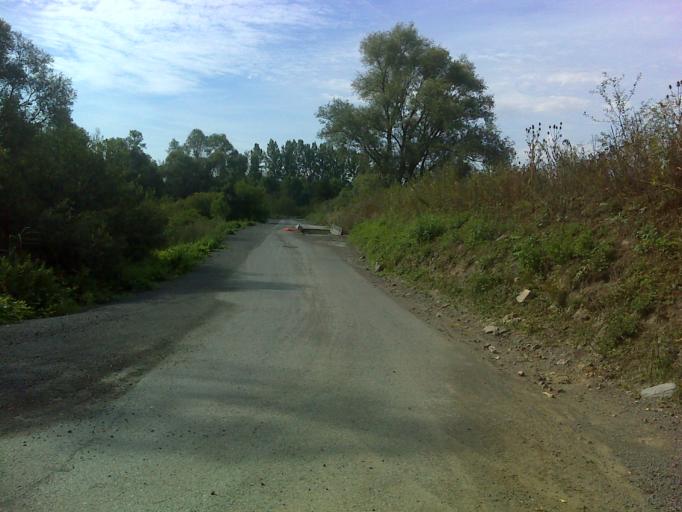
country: FR
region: Nord-Pas-de-Calais
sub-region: Departement du Nord
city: Conde-sur-l'Escaut
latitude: 50.4495
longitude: 3.6140
